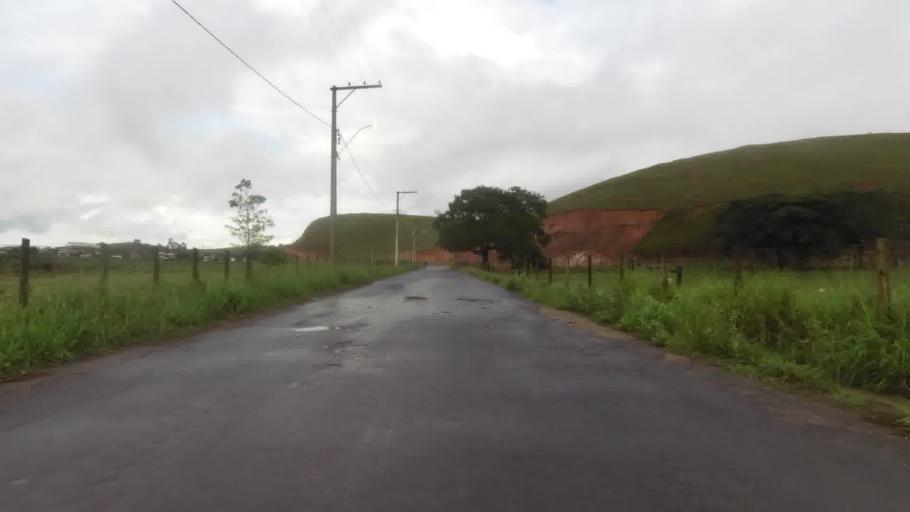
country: BR
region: Espirito Santo
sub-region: Alfredo Chaves
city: Alfredo Chaves
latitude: -20.6880
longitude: -40.6804
